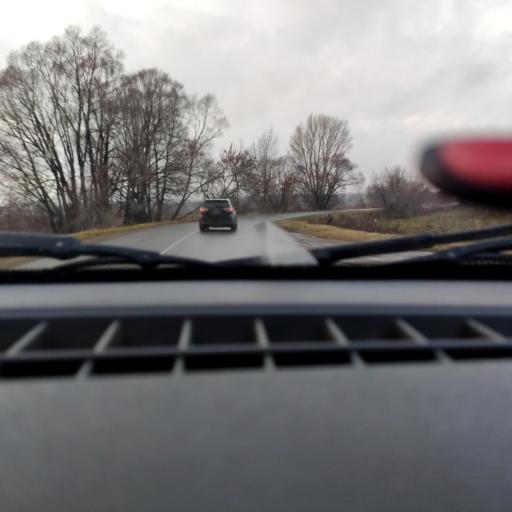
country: RU
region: Bashkortostan
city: Avdon
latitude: 54.5030
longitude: 55.8789
